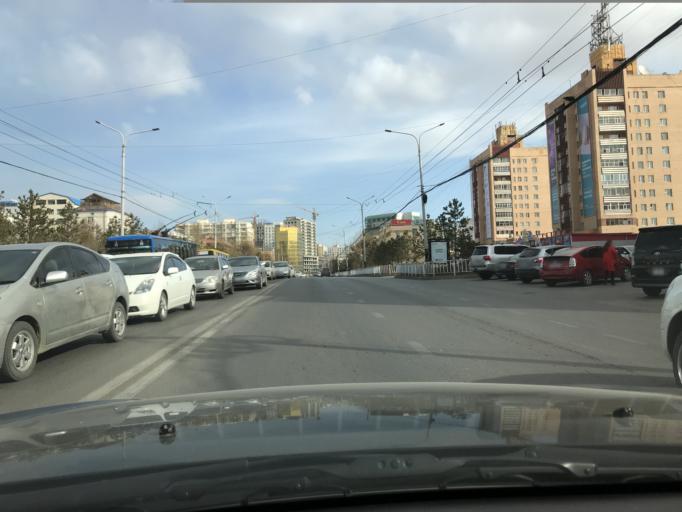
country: MN
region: Ulaanbaatar
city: Ulaanbaatar
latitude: 47.9186
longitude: 106.9369
